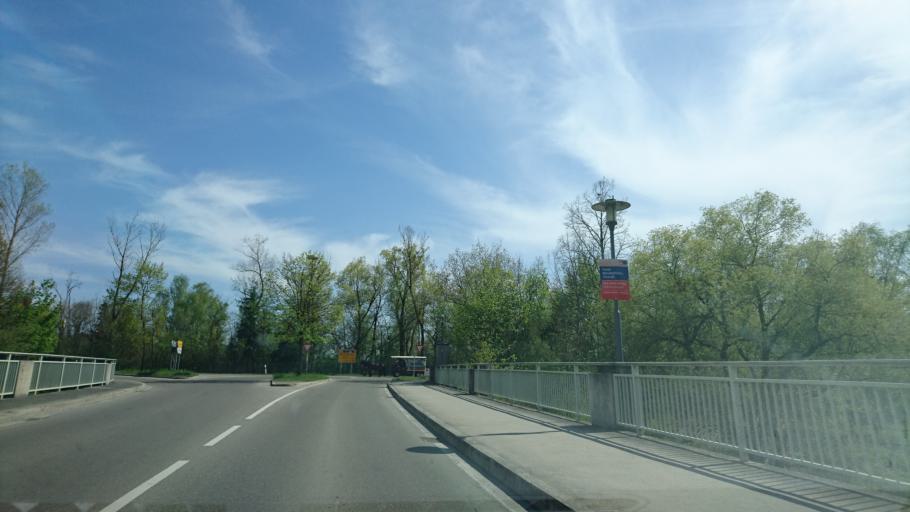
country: DE
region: Bavaria
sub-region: Swabia
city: Offingen
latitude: 48.4853
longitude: 10.3791
